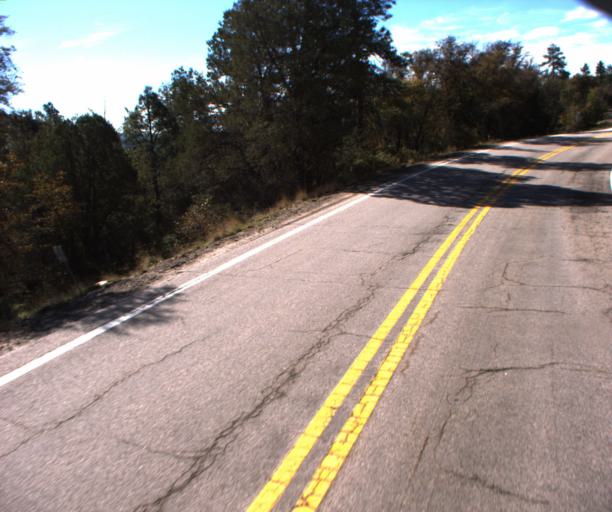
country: US
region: Arizona
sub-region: Yavapai County
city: Prescott
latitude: 34.4412
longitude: -112.5476
